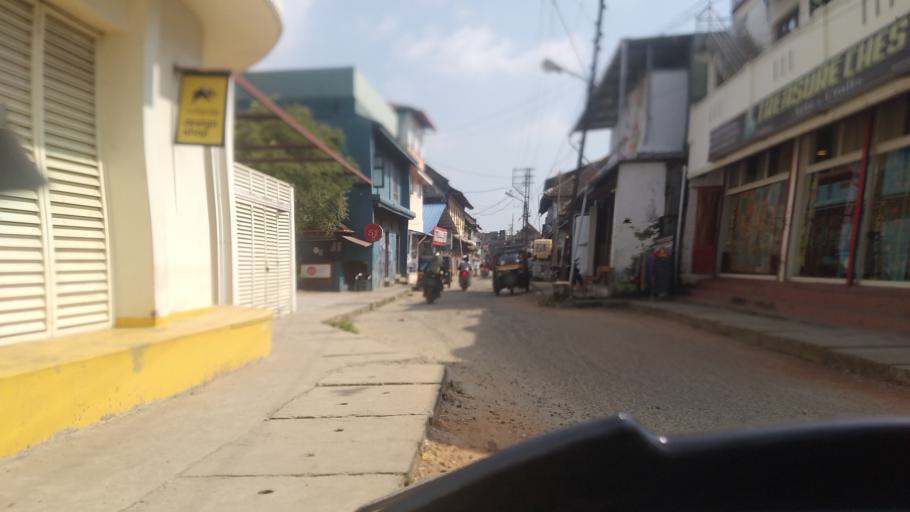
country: IN
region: Kerala
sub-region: Ernakulam
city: Cochin
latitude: 9.9666
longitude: 76.2532
